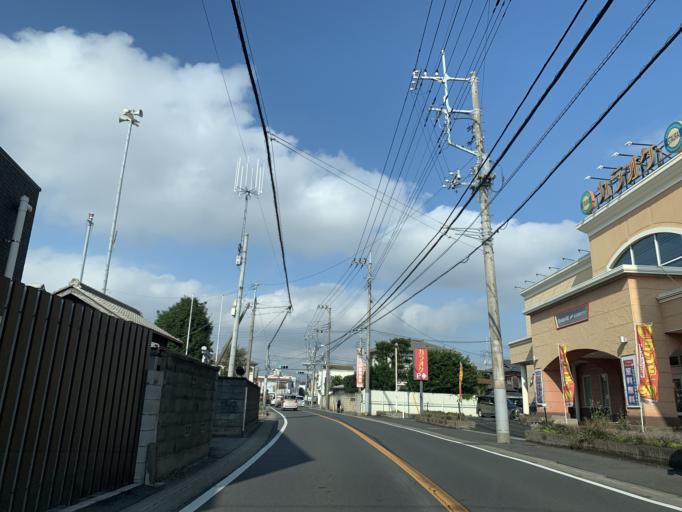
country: JP
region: Chiba
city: Noda
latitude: 35.9119
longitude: 139.9051
